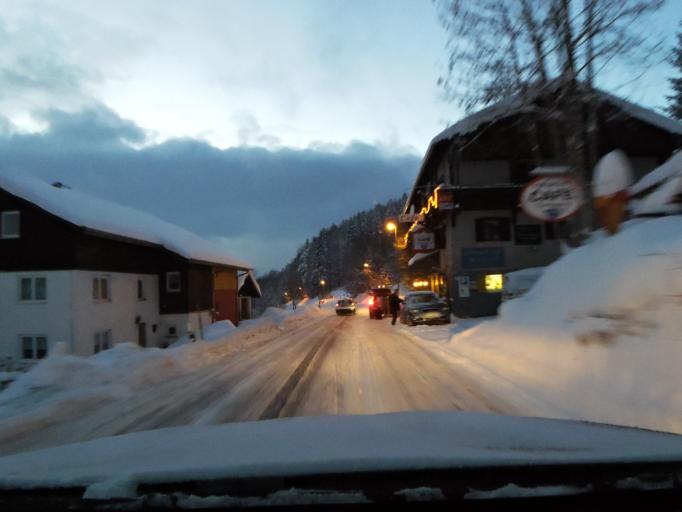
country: DE
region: Bavaria
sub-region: Lower Bavaria
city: Spiegelau
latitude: 48.9113
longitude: 13.3468
